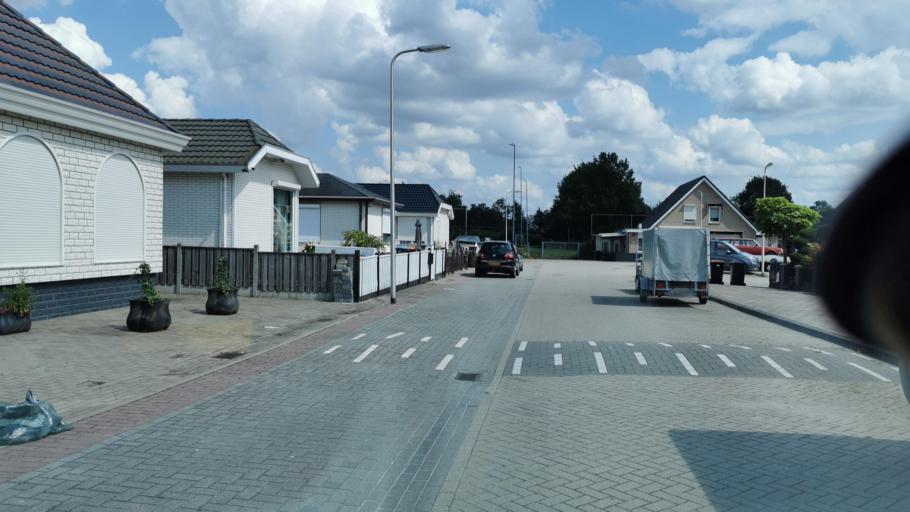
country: NL
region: Overijssel
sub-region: Gemeente Enschede
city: Enschede
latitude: 52.2219
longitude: 6.9369
